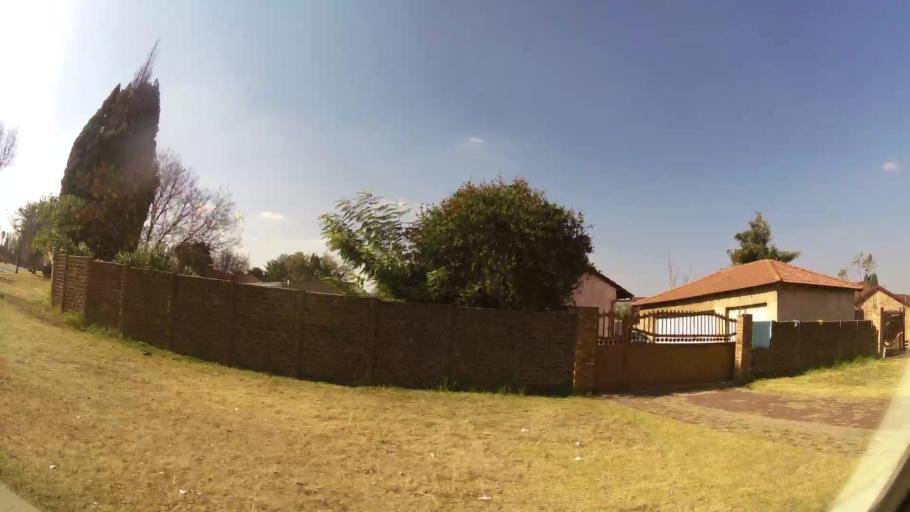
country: ZA
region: Gauteng
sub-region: Ekurhuleni Metropolitan Municipality
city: Benoni
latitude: -26.2435
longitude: 28.3109
